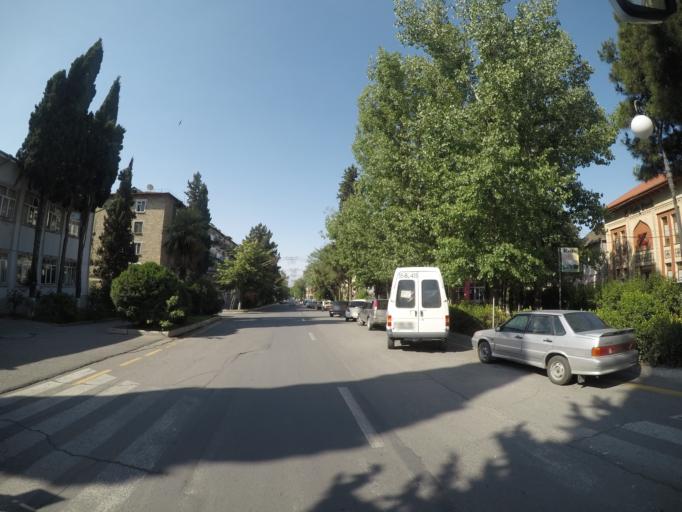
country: AZ
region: Shaki City
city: Sheki
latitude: 41.2028
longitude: 47.1781
